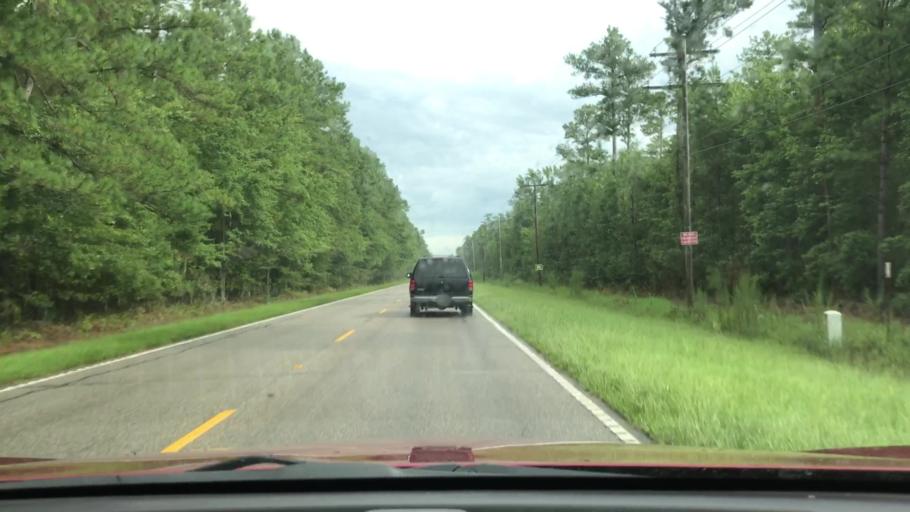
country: US
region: South Carolina
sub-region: Georgetown County
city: Georgetown
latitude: 33.4432
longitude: -79.2775
